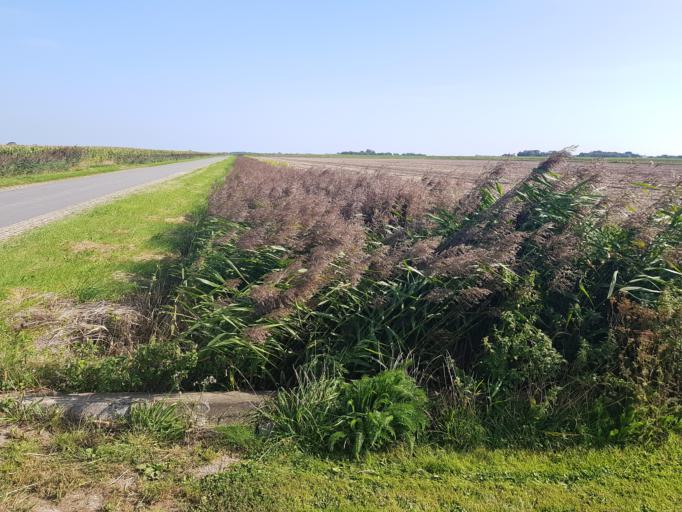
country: NL
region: North Holland
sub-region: Gemeente Texel
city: Den Burg
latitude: 53.1122
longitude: 4.8609
